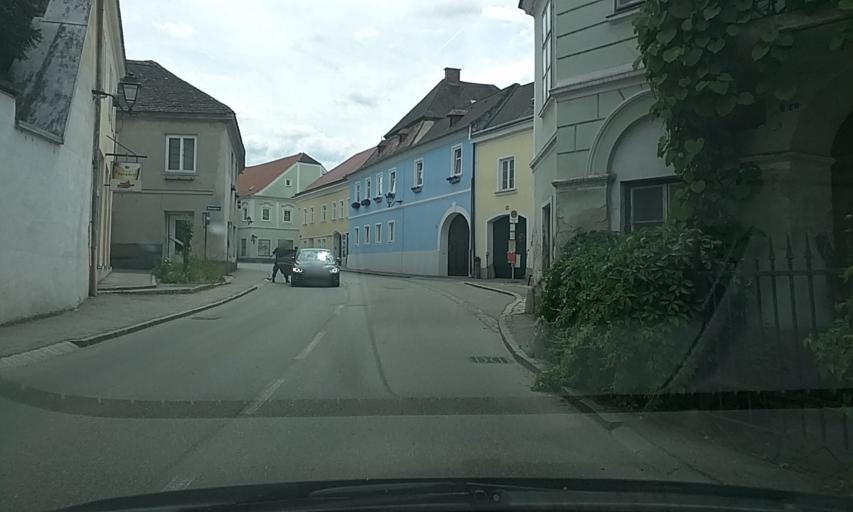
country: AT
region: Lower Austria
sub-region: Politischer Bezirk Krems
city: Weinzierl bei Krems
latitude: 48.3943
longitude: 15.5765
